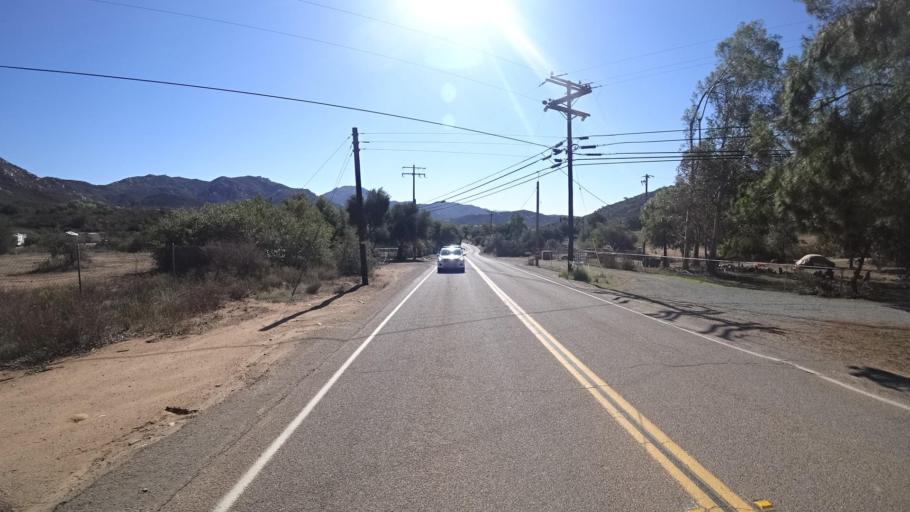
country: US
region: California
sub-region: San Diego County
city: Jamul
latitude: 32.7300
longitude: -116.8201
